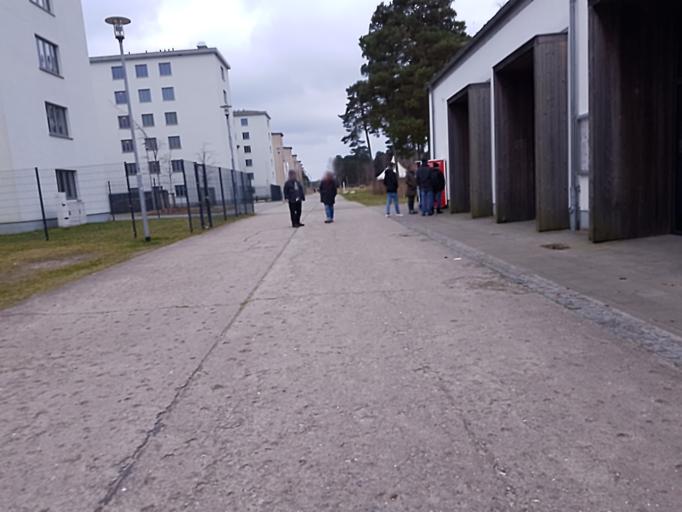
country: DE
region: Mecklenburg-Vorpommern
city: Ostseebad Binz
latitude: 54.4516
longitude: 13.5691
